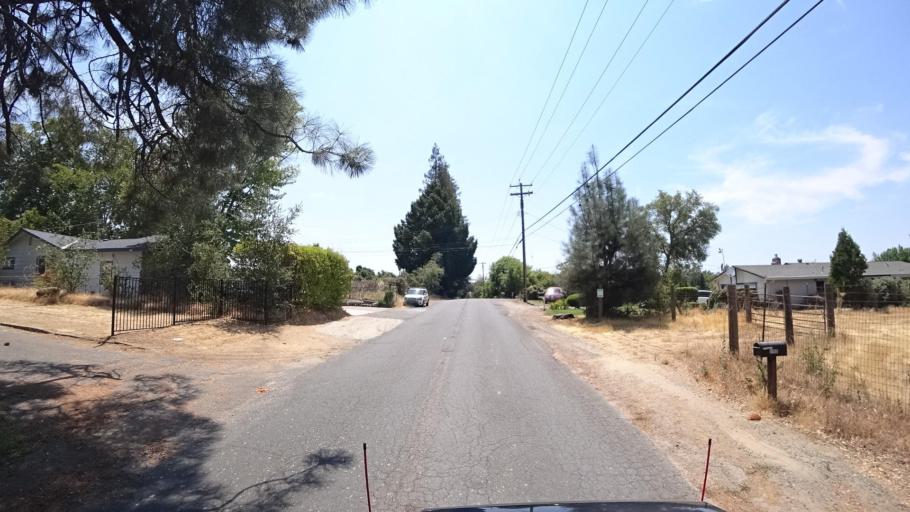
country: US
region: California
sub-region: Placer County
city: Loomis
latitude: 38.8180
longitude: -121.2195
